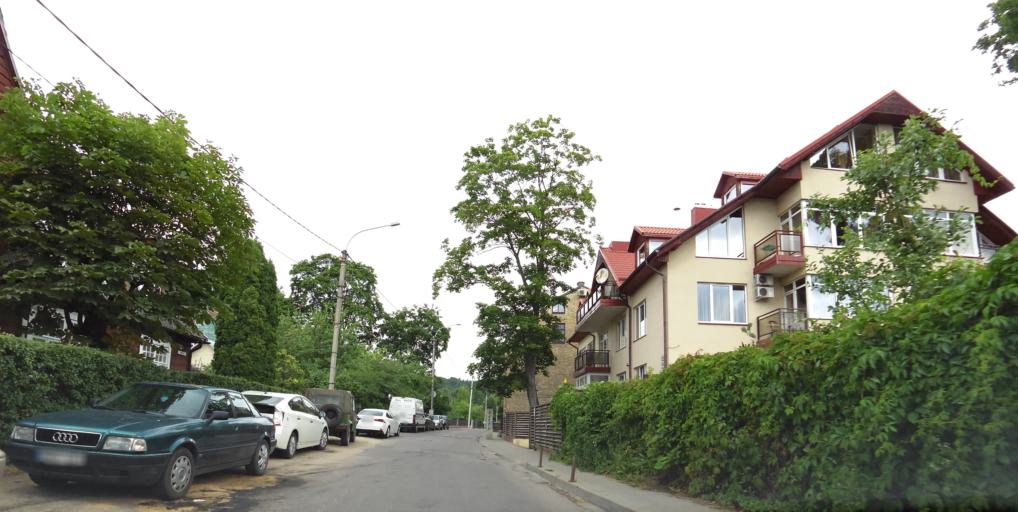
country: LT
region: Vilnius County
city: Seskine
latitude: 54.6930
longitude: 25.2455
